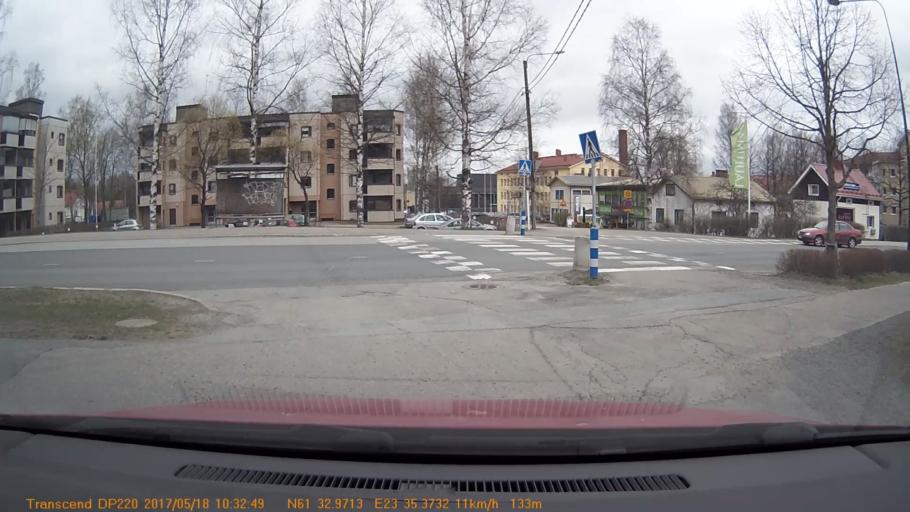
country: FI
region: Pirkanmaa
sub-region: Tampere
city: Yloejaervi
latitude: 61.5495
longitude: 23.5893
